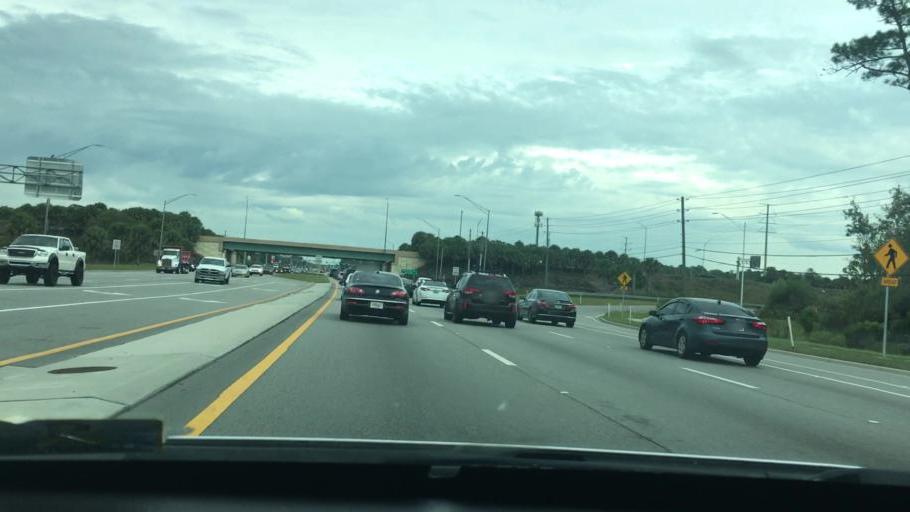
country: US
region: Florida
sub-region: Orange County
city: Alafaya
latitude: 28.5654
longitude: -81.1932
